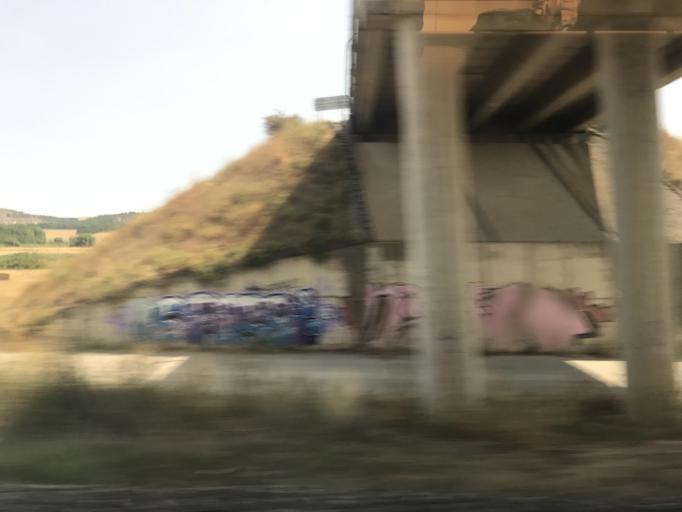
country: ES
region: Castille and Leon
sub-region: Provincia de Burgos
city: Villaquiran de los Infantes
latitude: 42.2174
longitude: -3.9976
